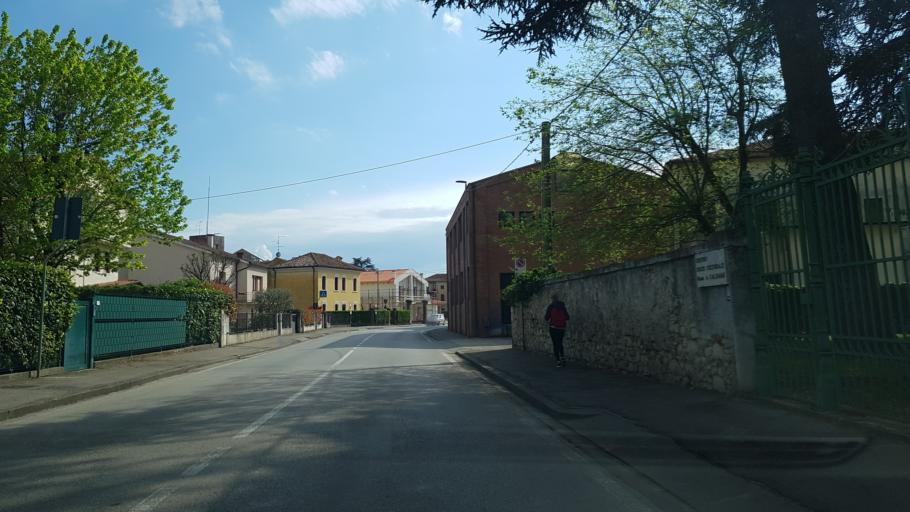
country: IT
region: Veneto
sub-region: Provincia di Vicenza
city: Lonigo
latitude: 45.3875
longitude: 11.3928
